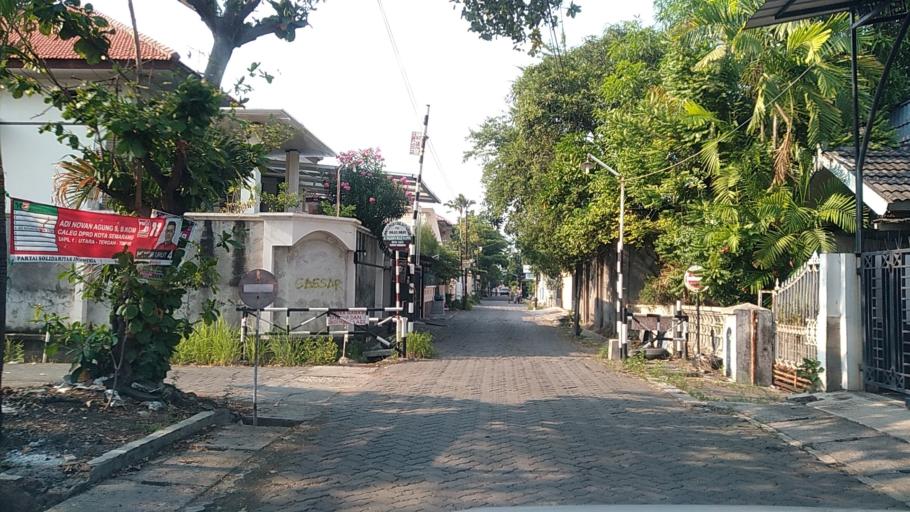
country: ID
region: Central Java
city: Semarang
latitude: -6.9574
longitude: 110.4074
